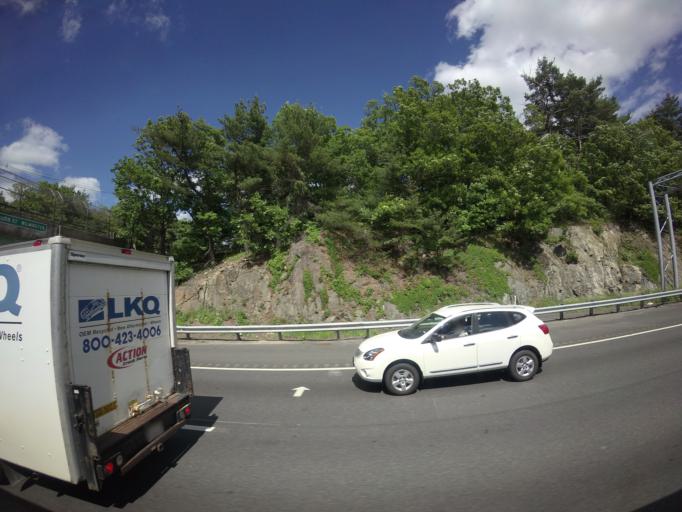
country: US
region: Massachusetts
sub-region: Middlesex County
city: Wilmington
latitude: 42.5692
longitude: -71.1465
